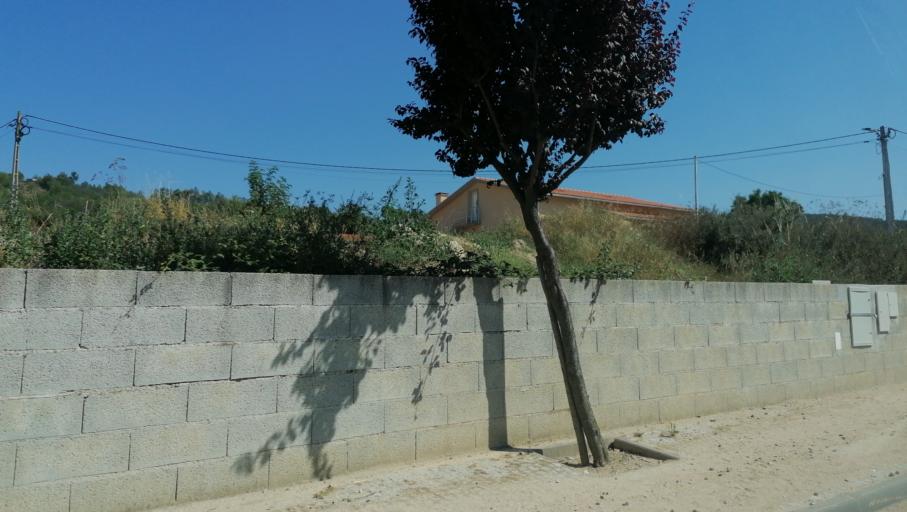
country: PT
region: Viseu
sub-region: Tarouca
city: Tarouca
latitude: 41.0222
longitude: -7.7689
